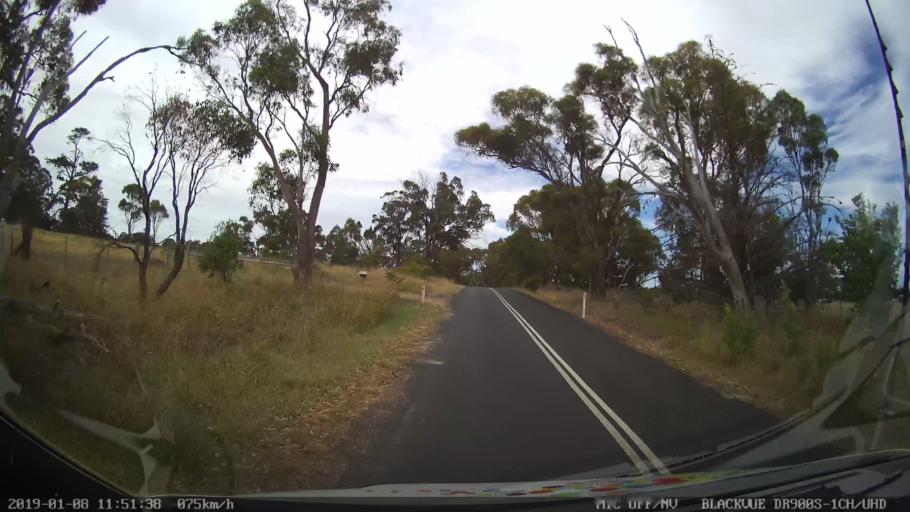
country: AU
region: New South Wales
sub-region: Armidale Dumaresq
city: Armidale
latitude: -30.3951
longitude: 151.5607
